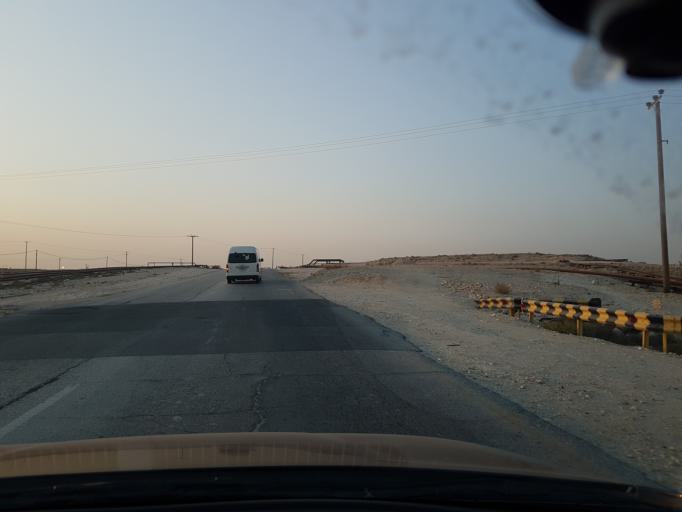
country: BH
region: Central Governorate
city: Dar Kulayb
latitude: 26.0544
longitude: 50.5560
